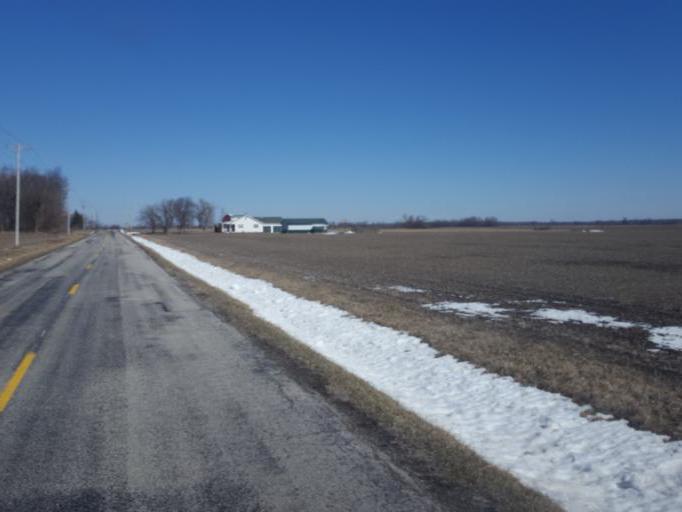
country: US
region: Ohio
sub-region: Wyandot County
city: Upper Sandusky
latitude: 40.6784
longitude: -83.2978
